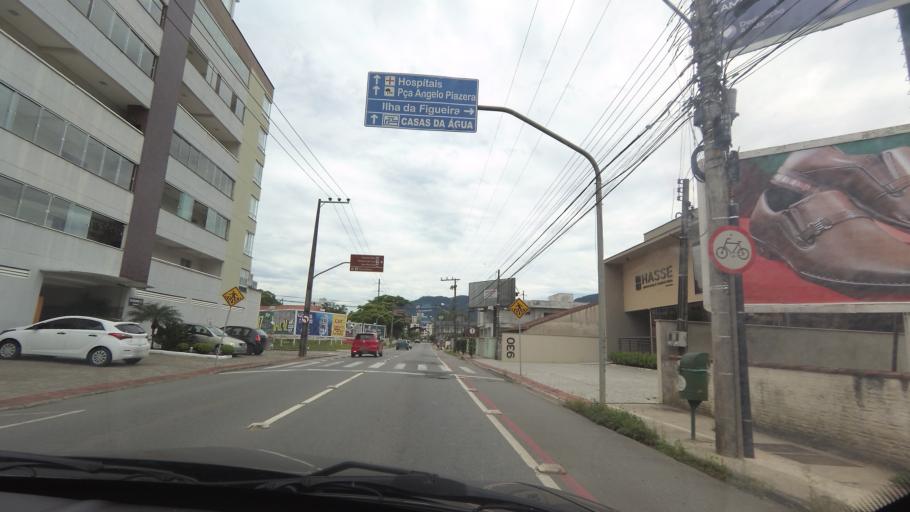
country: BR
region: Santa Catarina
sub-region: Jaragua Do Sul
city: Jaragua do Sul
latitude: -26.4989
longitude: -49.0808
